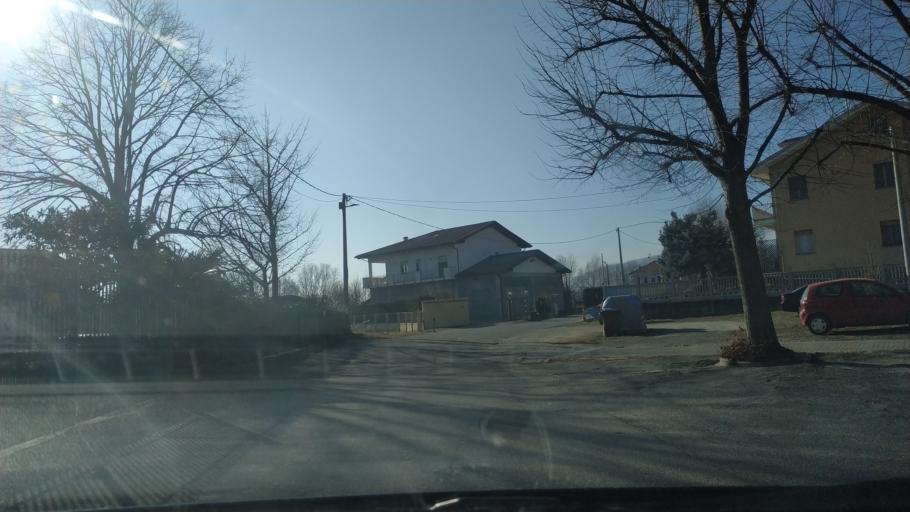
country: IT
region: Piedmont
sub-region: Provincia di Torino
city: Montalto Dora
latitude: 45.4878
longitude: 7.8610
